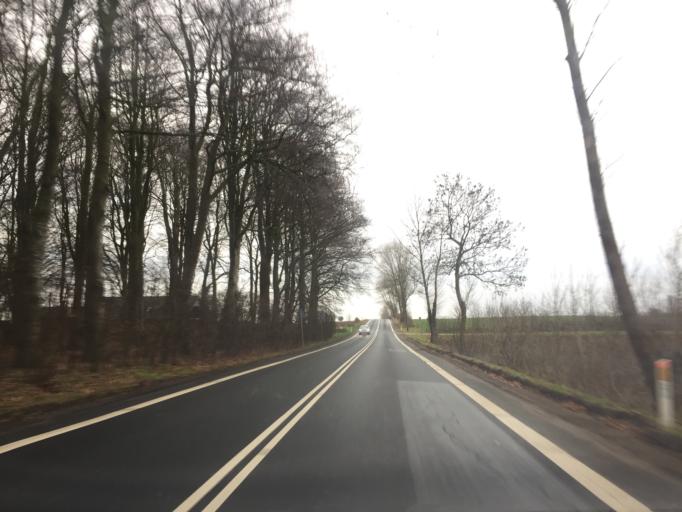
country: DK
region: South Denmark
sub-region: Svendborg Kommune
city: Thuro By
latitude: 55.1502
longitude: 10.6731
